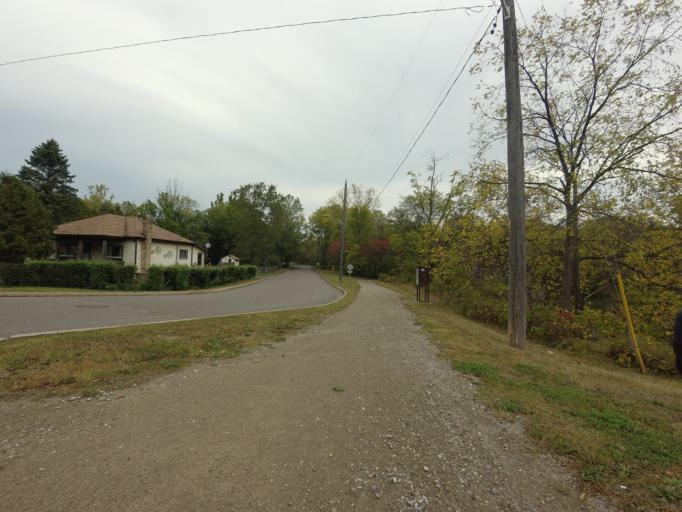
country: CA
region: Ontario
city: Brantford
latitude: 43.1378
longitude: -80.2212
